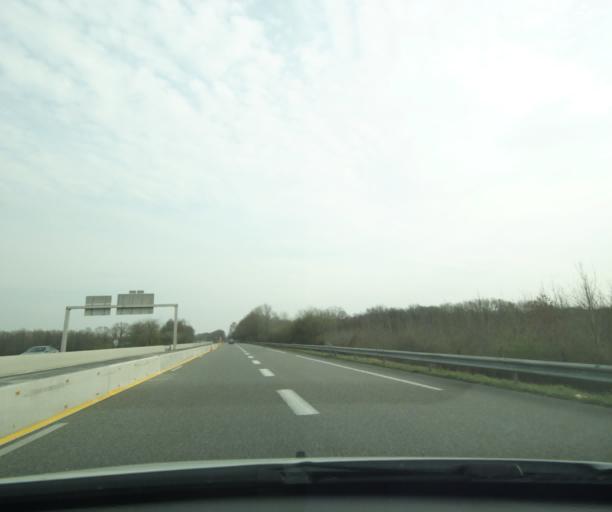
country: FR
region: Aquitaine
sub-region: Departement des Pyrenees-Atlantiques
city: Artix
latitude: 43.3942
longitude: -0.5454
